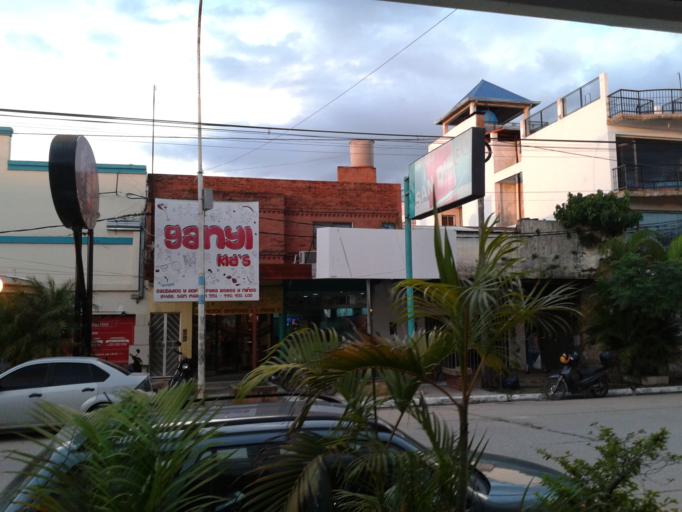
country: AR
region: Formosa
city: Clorinda
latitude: -25.2870
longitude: -57.7122
